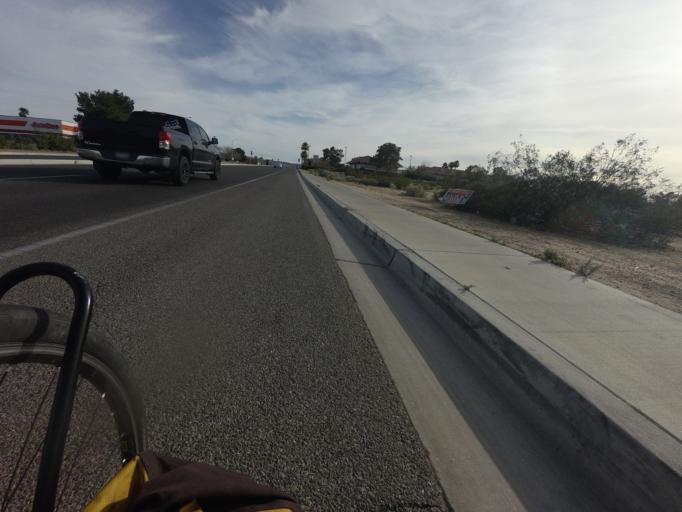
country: US
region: California
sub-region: Kern County
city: Ridgecrest
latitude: 35.6394
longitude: -117.6699
